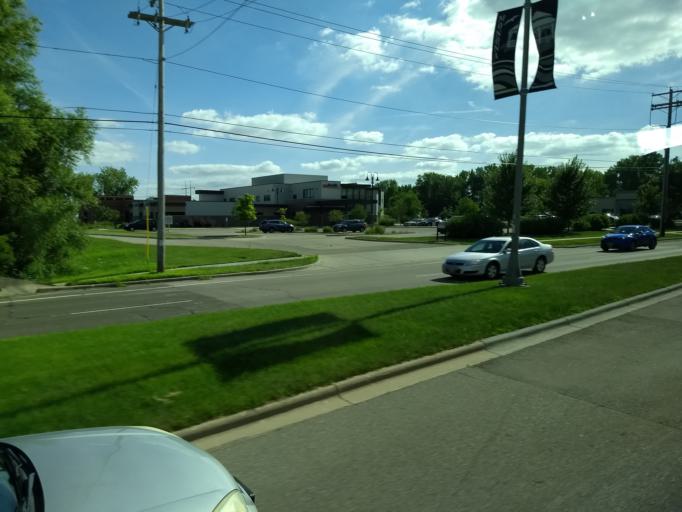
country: US
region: Wisconsin
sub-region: Dane County
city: Monona
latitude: 43.0482
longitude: -89.3135
